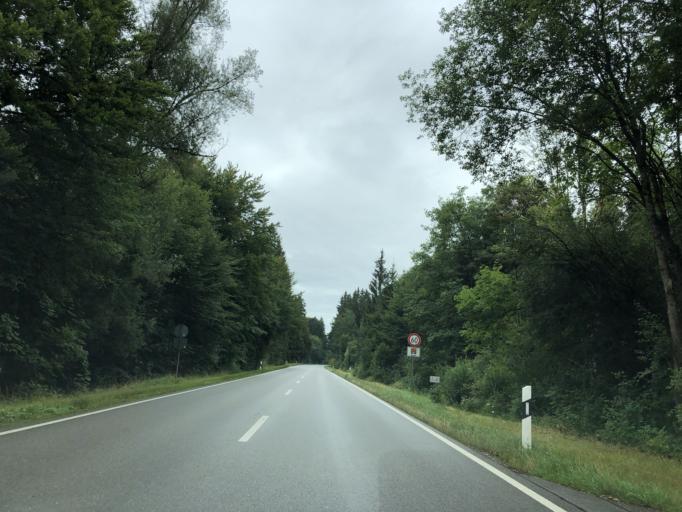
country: DE
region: Bavaria
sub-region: Upper Bavaria
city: Sauerlach
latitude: 48.0076
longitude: 11.6382
